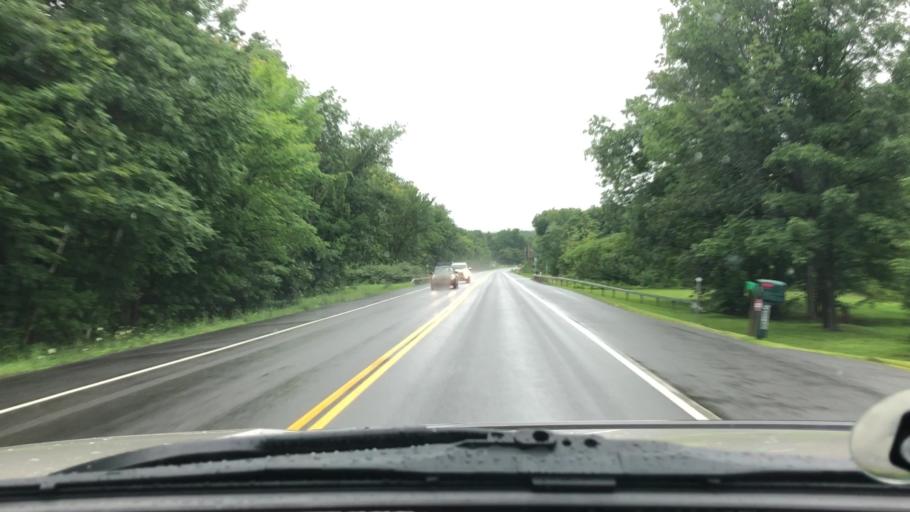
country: US
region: New York
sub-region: Greene County
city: Cairo
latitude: 42.3204
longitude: -74.0844
